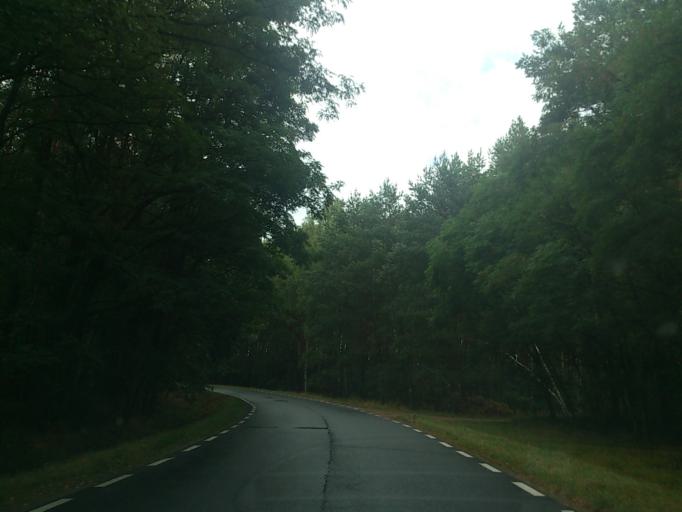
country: PL
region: Greater Poland Voivodeship
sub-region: Powiat poznanski
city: Pobiedziska
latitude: 52.5140
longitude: 17.1989
